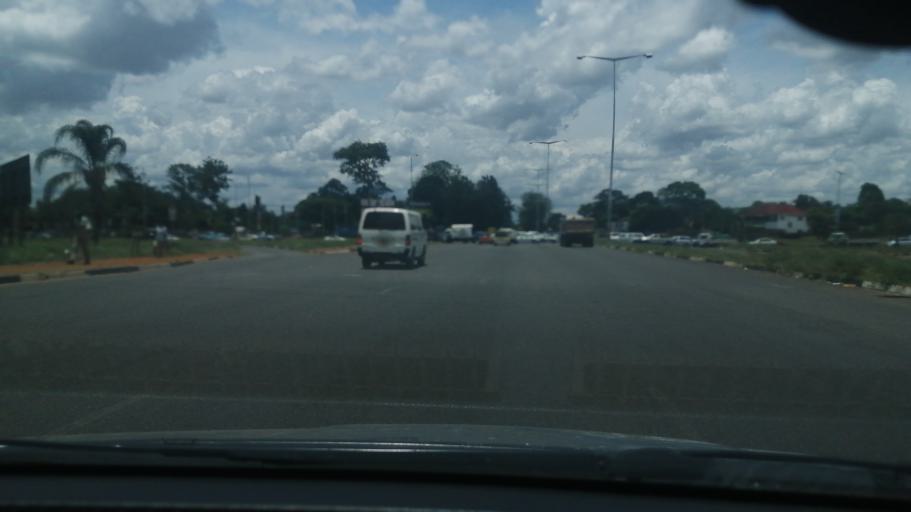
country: ZW
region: Harare
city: Harare
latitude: -17.8297
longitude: 31.0341
